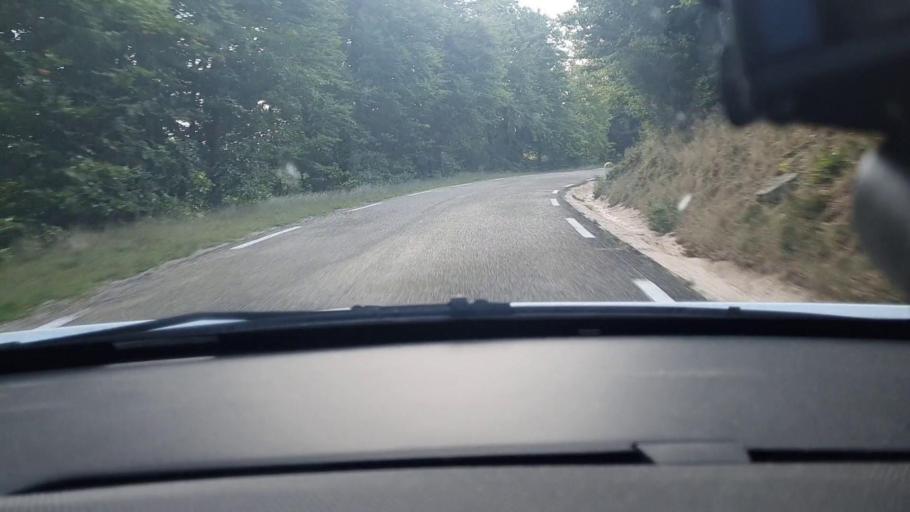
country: FR
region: Languedoc-Roussillon
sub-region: Departement du Gard
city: Branoux-les-Taillades
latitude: 44.3752
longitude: 3.9124
